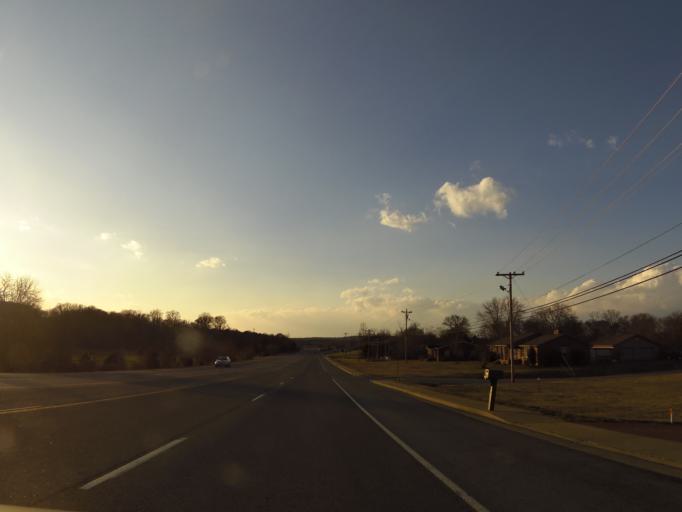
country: US
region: Tennessee
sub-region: Wilson County
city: Lebanon
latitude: 36.2323
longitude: -86.3835
